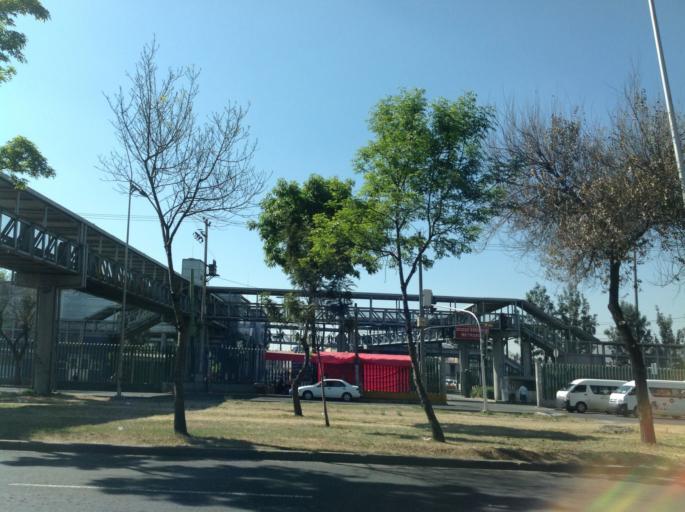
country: MX
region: Mexico
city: Ciudad Nezahualcoyotl
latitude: 19.3912
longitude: -99.0466
